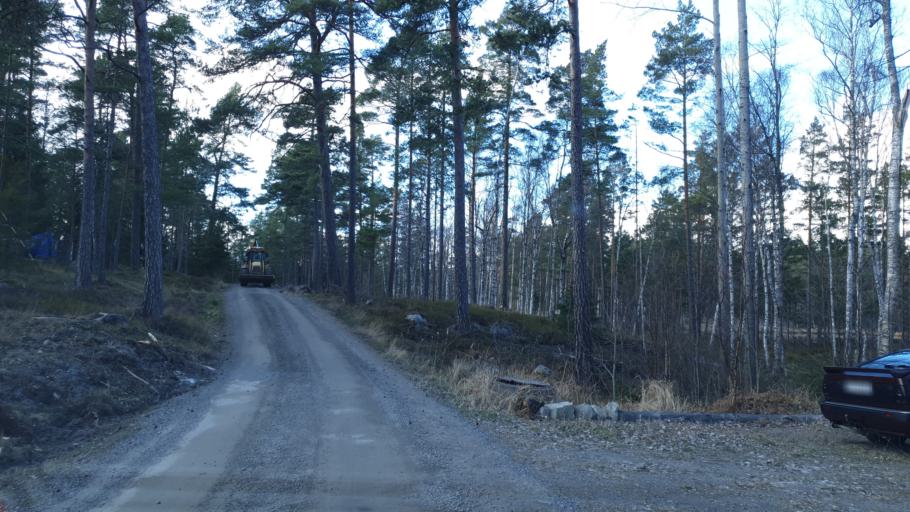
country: SE
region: Stockholm
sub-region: Varmdo Kommun
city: Holo
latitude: 59.2713
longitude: 18.6393
